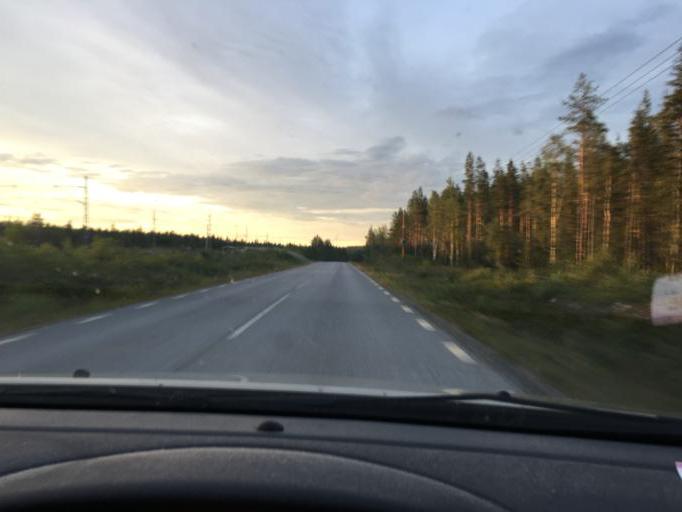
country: SE
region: Norrbotten
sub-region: Lulea Kommun
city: Ranea
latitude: 66.0461
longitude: 22.3468
